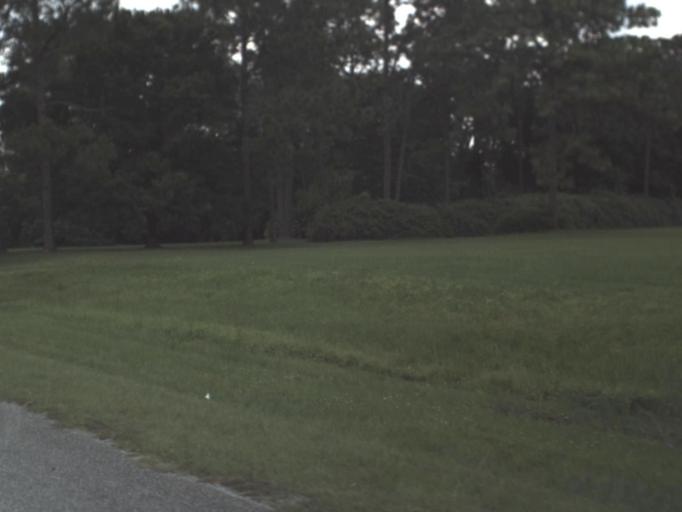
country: US
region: Florida
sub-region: Putnam County
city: Palatka
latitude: 29.6114
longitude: -81.7117
